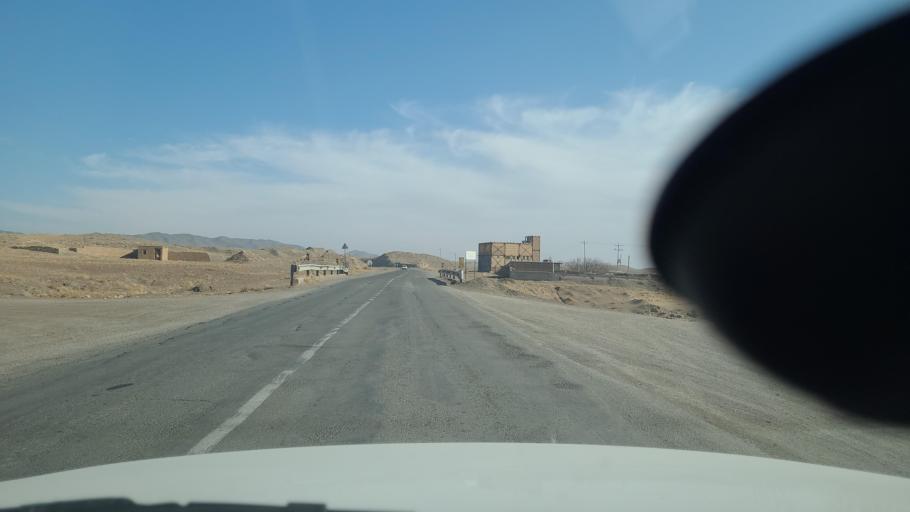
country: IR
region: Razavi Khorasan
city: Fariman
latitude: 35.5929
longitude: 59.6853
